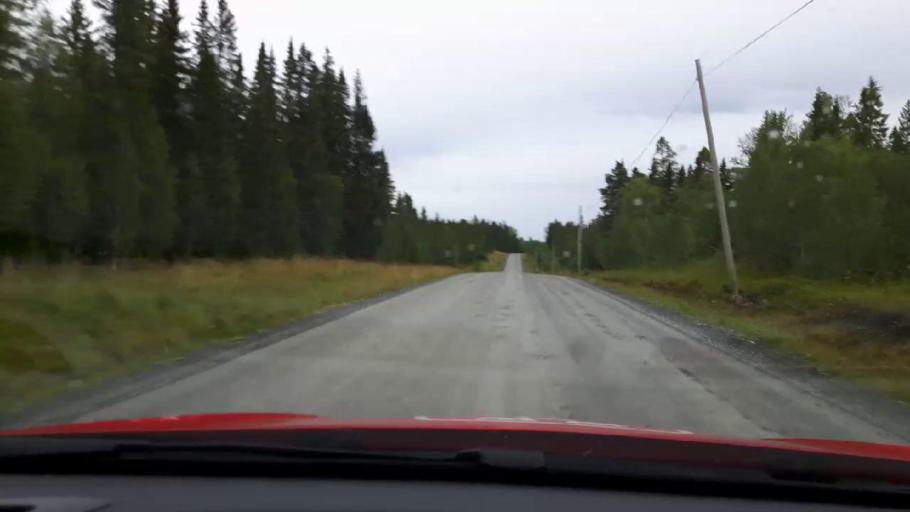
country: SE
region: Jaemtland
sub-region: Are Kommun
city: Jarpen
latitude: 63.4222
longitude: 13.3463
